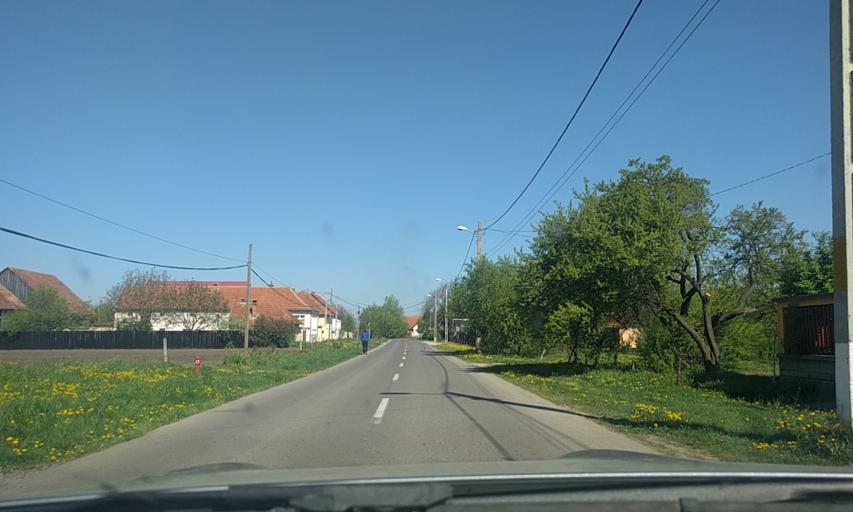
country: RO
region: Brasov
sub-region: Comuna Bod
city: Colonia Bod
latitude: 45.7071
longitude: 25.5709
